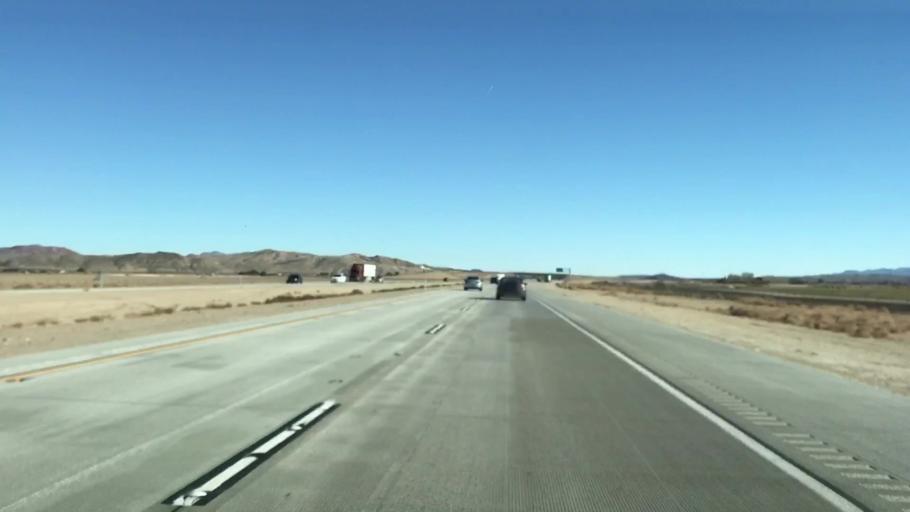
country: US
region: California
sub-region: San Bernardino County
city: Lenwood
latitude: 34.9154
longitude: -117.1330
